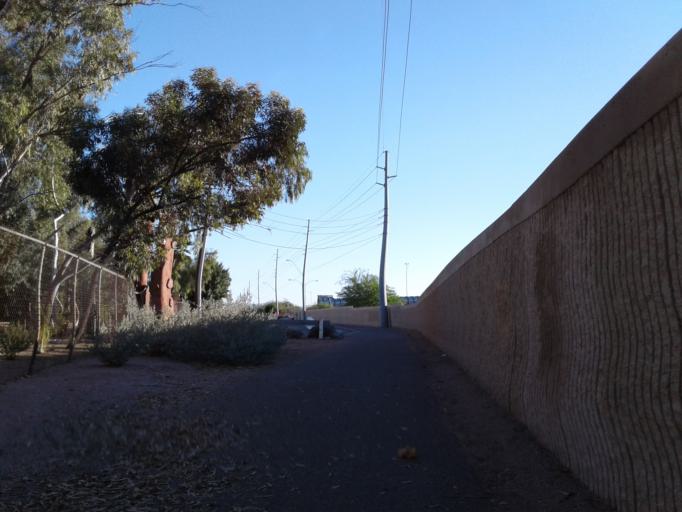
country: US
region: Arizona
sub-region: Maricopa County
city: Paradise Valley
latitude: 33.6320
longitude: -112.0049
